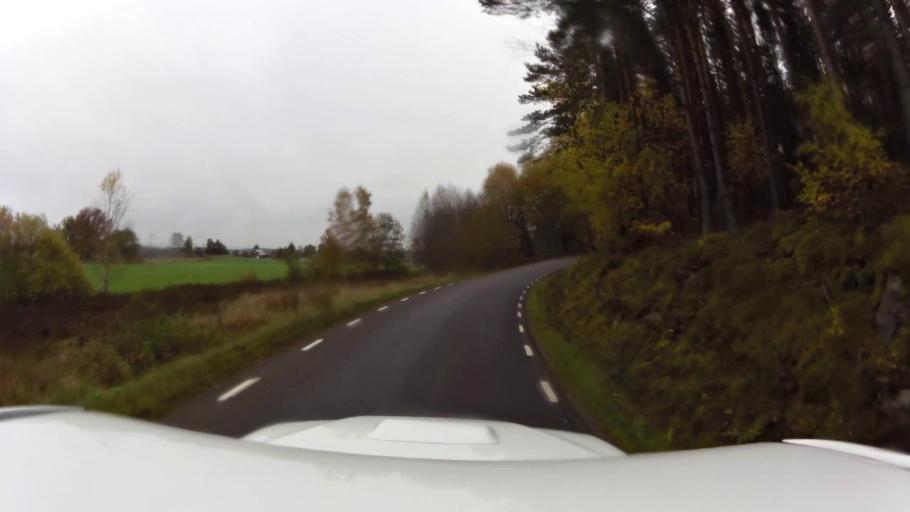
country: SE
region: OEstergoetland
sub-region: Linkopings Kommun
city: Linghem
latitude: 58.3561
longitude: 15.8503
